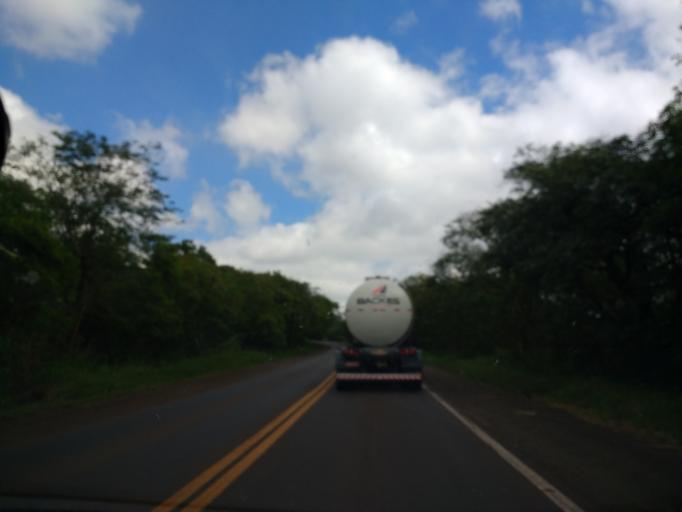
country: BR
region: Parana
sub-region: Cruzeiro Do Oeste
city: Cruzeiro do Oeste
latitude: -23.7894
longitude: -53.0339
